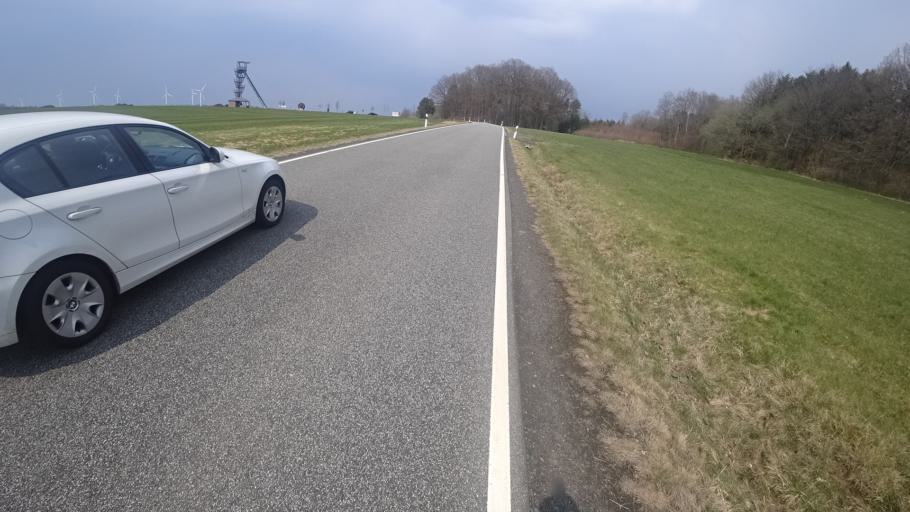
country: DE
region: Rheinland-Pfalz
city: Streithausen
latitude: 50.7195
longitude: 7.8241
